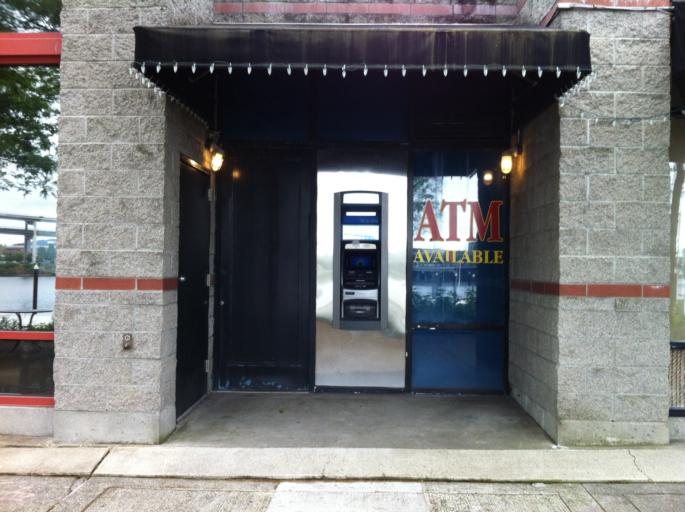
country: US
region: Oregon
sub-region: Multnomah County
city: Portland
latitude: 45.5099
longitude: -122.6734
